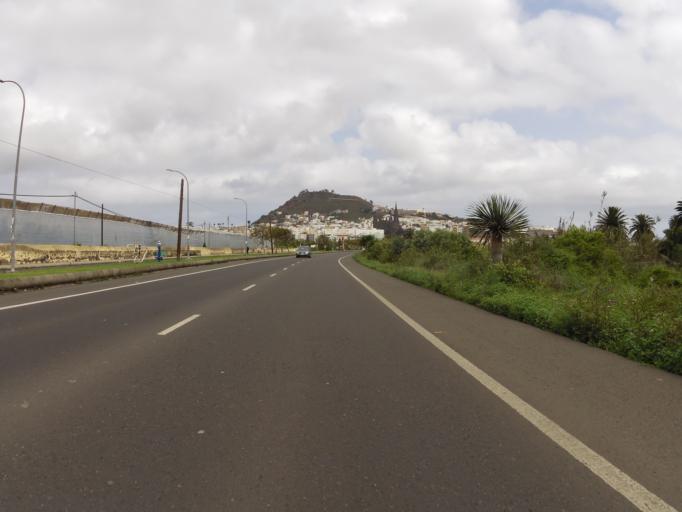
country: ES
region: Canary Islands
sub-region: Provincia de Las Palmas
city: Arucas
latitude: 28.1115
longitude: -15.5258
